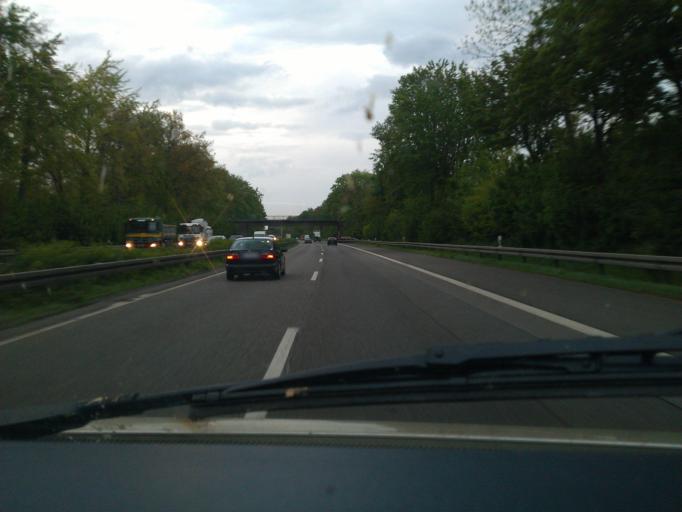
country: DE
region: North Rhine-Westphalia
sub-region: Regierungsbezirk Koln
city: Alsdorf
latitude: 50.8370
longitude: 6.1903
